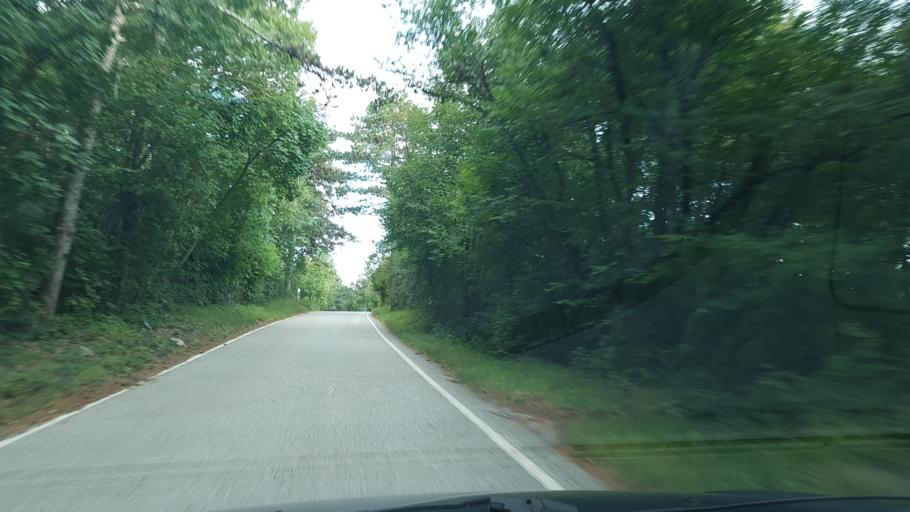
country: SI
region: Rence-Vogrsko
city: Rence
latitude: 45.8609
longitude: 13.6652
